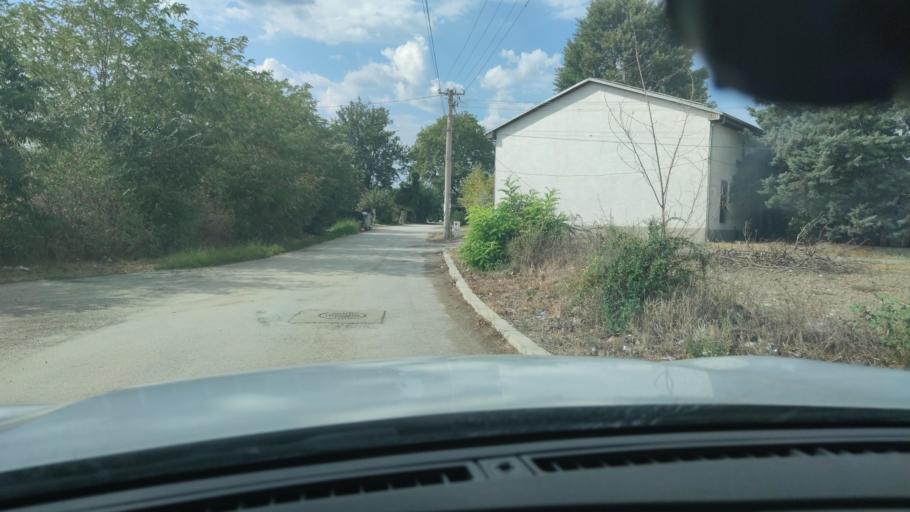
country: MK
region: Gevgelija
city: Gevgelija
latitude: 41.1643
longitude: 22.5052
